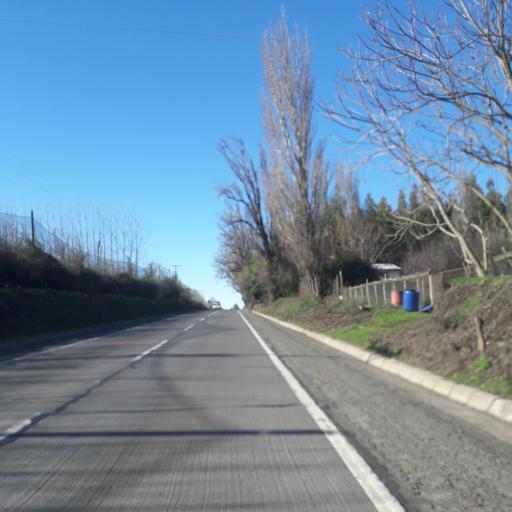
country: CL
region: Araucania
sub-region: Provincia de Malleco
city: Angol
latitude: -37.7513
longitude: -72.5867
